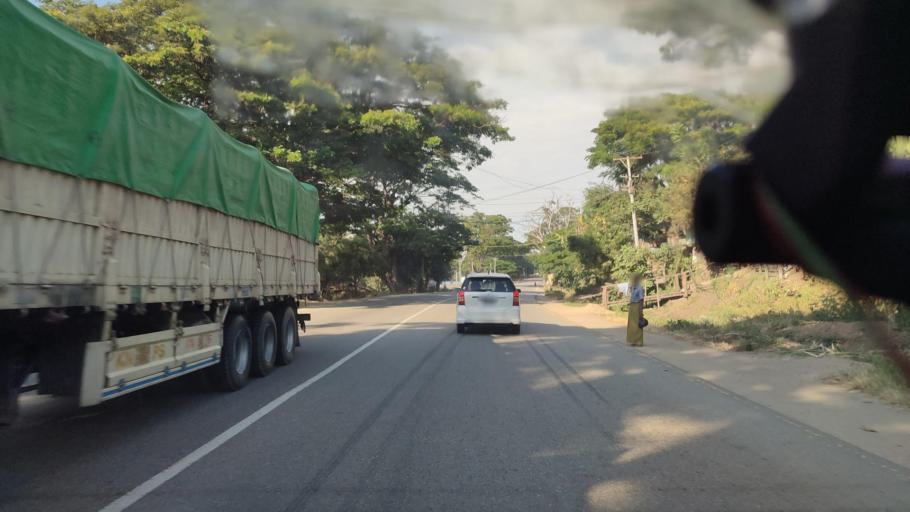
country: MM
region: Mandalay
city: Pyinmana
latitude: 20.0465
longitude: 96.2487
